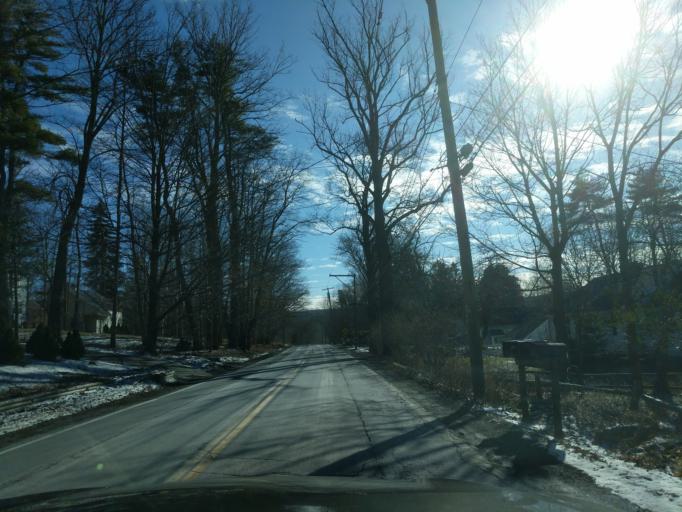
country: US
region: New York
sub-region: Tompkins County
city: East Ithaca
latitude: 42.4280
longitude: -76.4622
